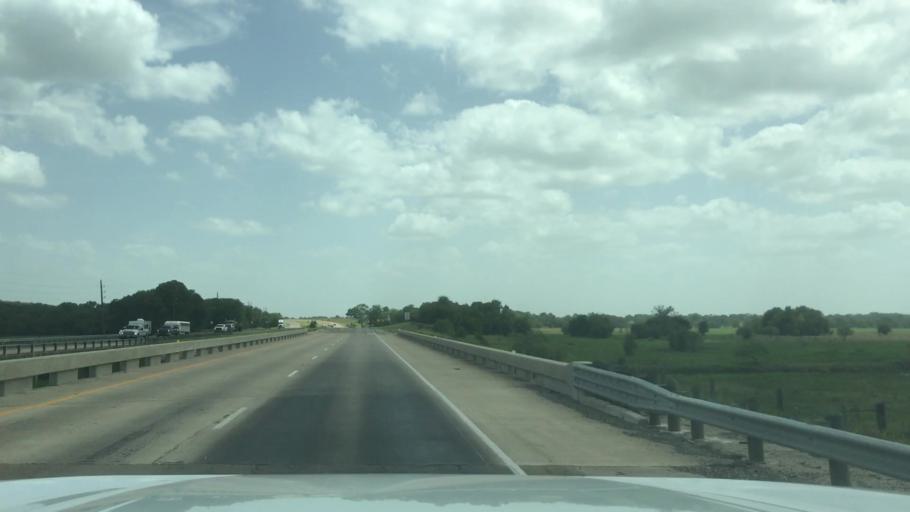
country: US
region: Texas
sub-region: Robertson County
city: Calvert
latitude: 31.0153
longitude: -96.7052
